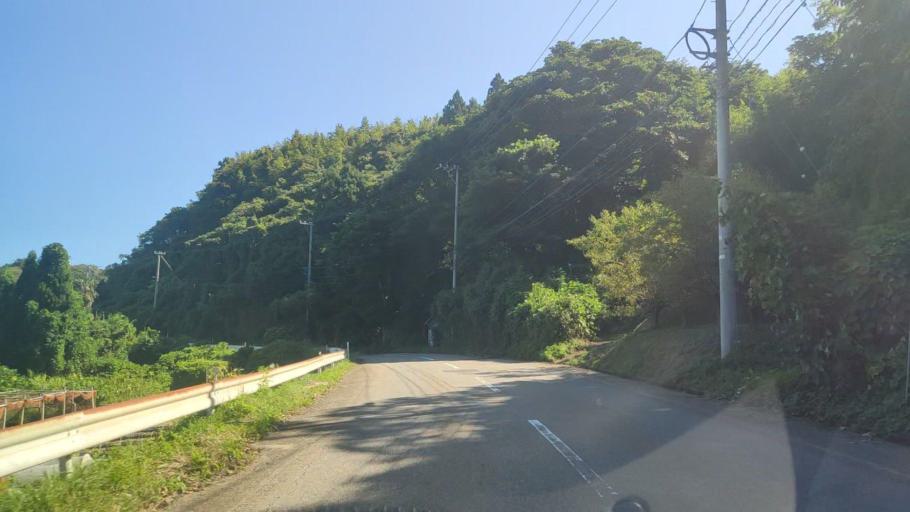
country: JP
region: Ishikawa
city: Nanao
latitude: 37.5195
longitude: 137.3273
